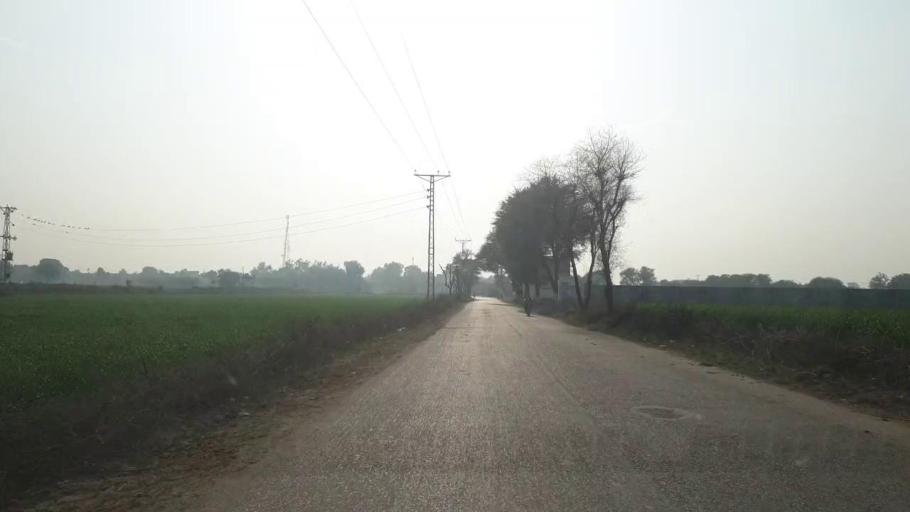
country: PK
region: Sindh
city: Hala
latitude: 25.7969
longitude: 68.3957
